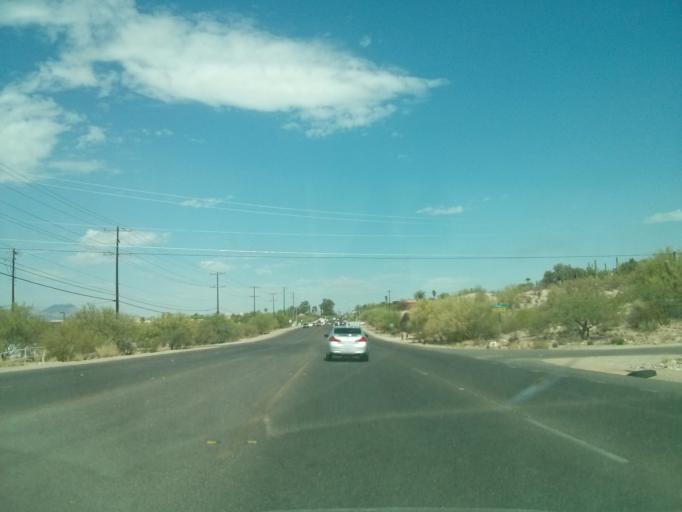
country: US
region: Arizona
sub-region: Pima County
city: Catalina Foothills
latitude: 32.2845
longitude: -110.9297
